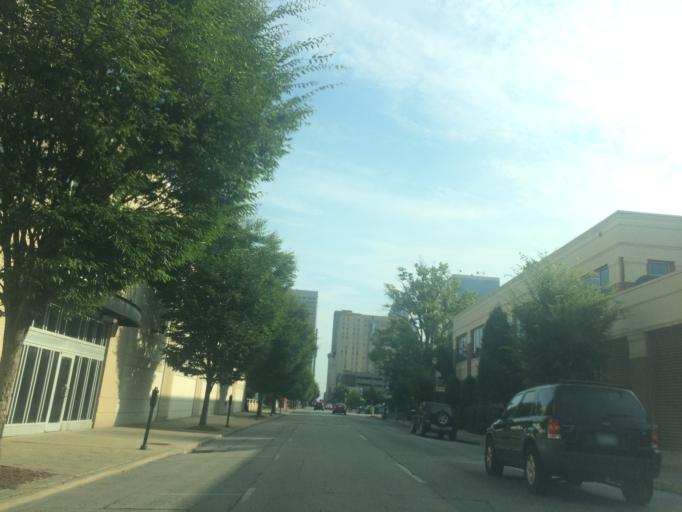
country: US
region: Kentucky
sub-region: Jefferson County
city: Louisville
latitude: 38.2473
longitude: -85.7599
